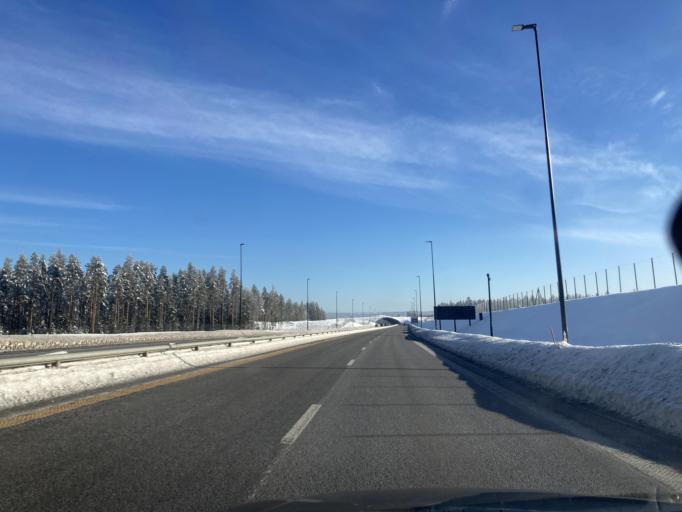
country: NO
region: Hedmark
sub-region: Elverum
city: Elverum
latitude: 60.8825
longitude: 11.4833
